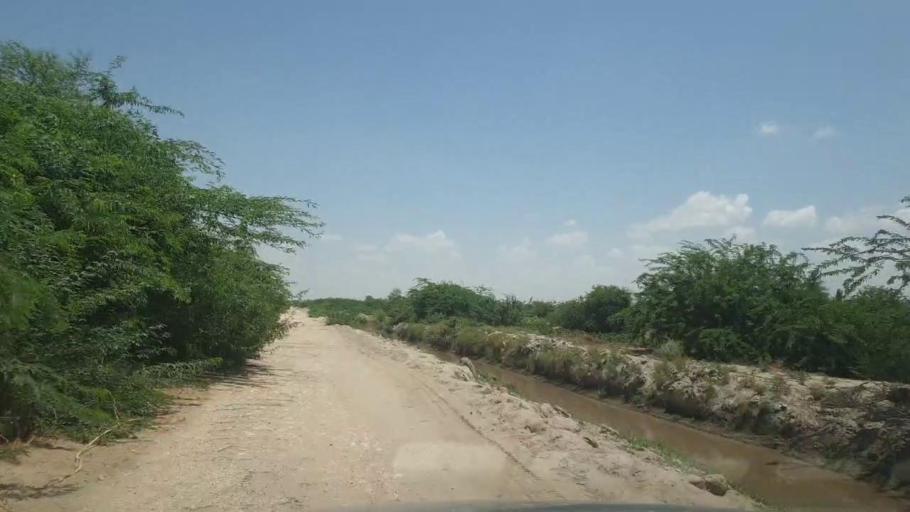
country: PK
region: Sindh
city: Kot Diji
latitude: 27.2903
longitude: 69.0637
